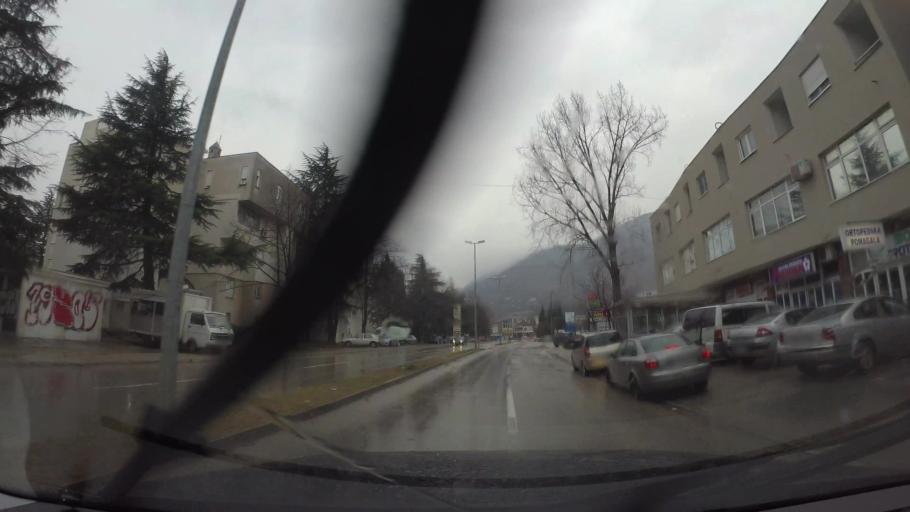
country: BA
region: Federation of Bosnia and Herzegovina
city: Cim
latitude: 43.3514
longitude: 17.7944
